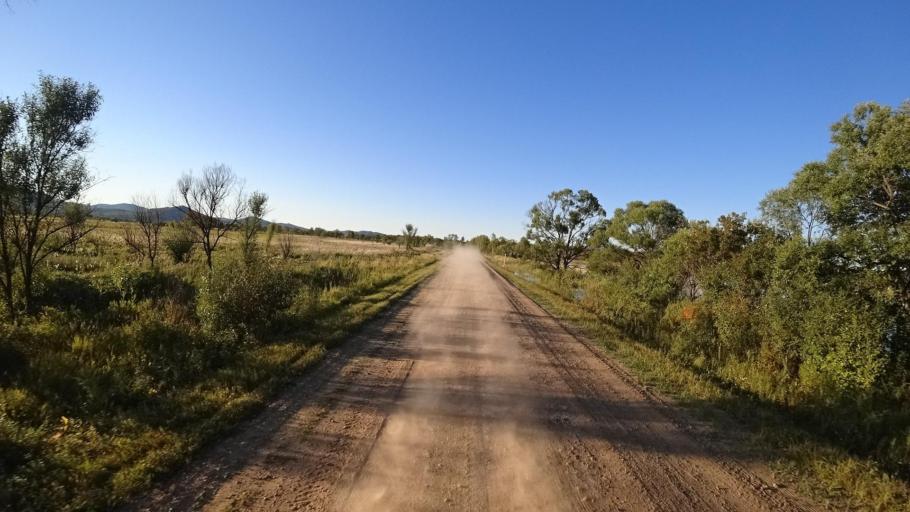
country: RU
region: Primorskiy
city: Kirovskiy
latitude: 44.8107
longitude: 133.6164
